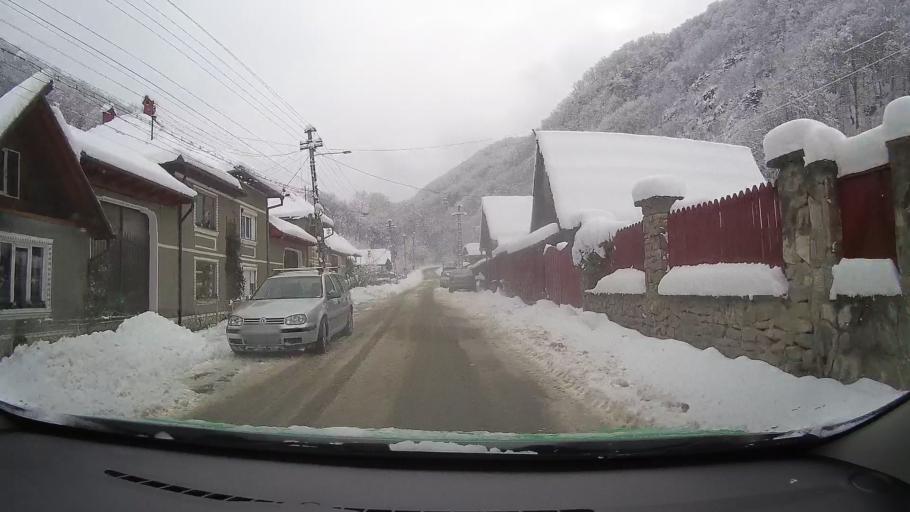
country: RO
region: Alba
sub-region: Comuna Sugag
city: Dobra
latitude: 45.7586
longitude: 23.6623
